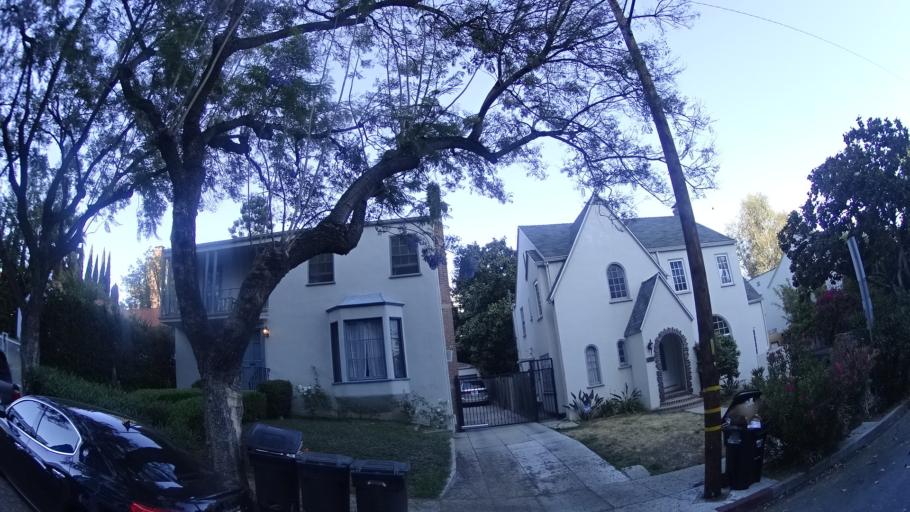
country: US
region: California
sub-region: Los Angeles County
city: Beverly Hills
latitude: 34.0897
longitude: -118.3921
